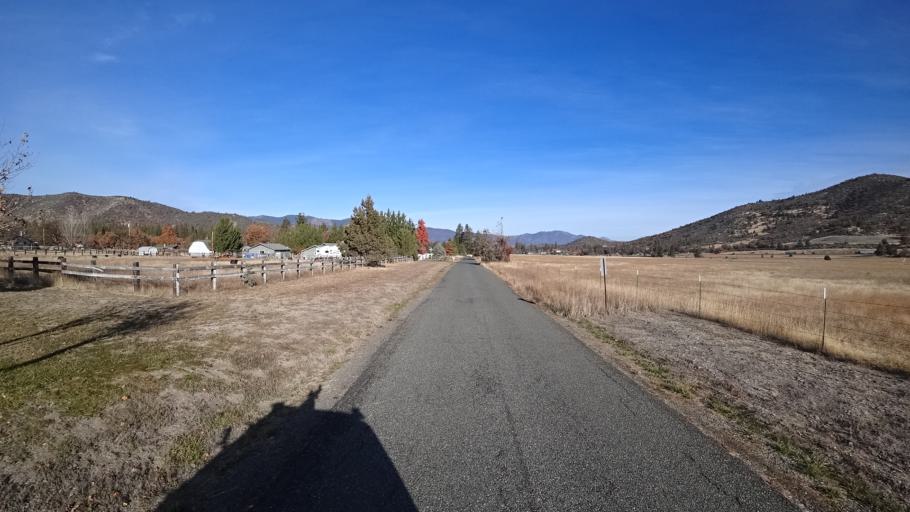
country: US
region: California
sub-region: Siskiyou County
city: Yreka
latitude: 41.6742
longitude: -122.6321
